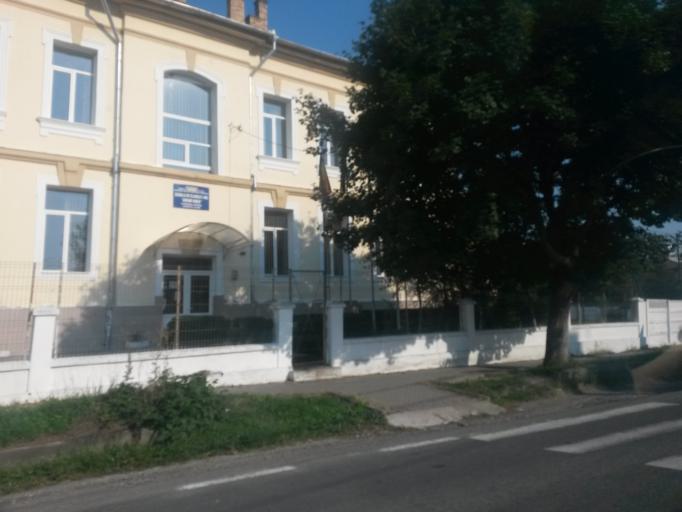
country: RO
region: Alba
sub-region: Comuna Unirea
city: Unirea
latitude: 46.4056
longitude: 23.8108
